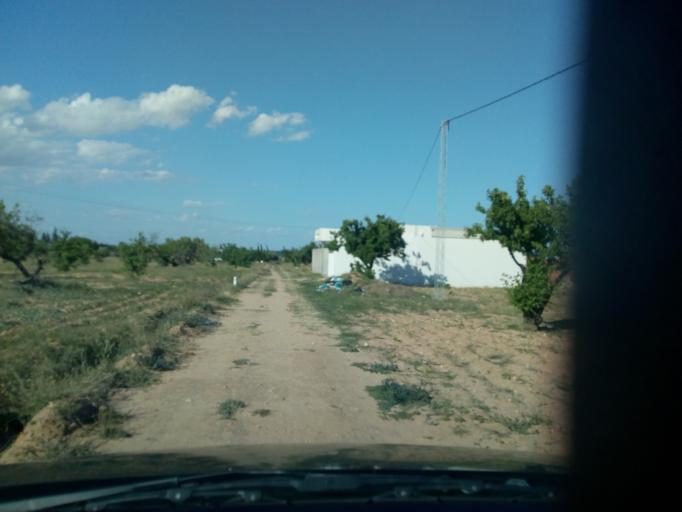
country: TN
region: Safaqis
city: Sfax
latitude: 34.7295
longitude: 10.6126
